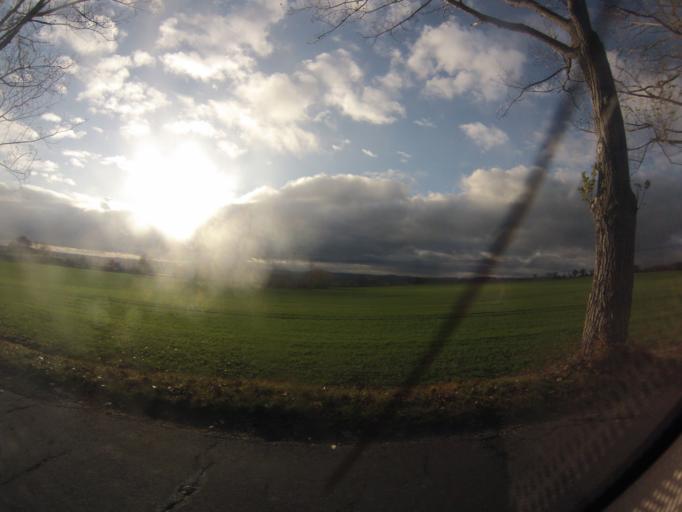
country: DE
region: Thuringia
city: Vollmershain
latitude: 50.8642
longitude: 12.2980
